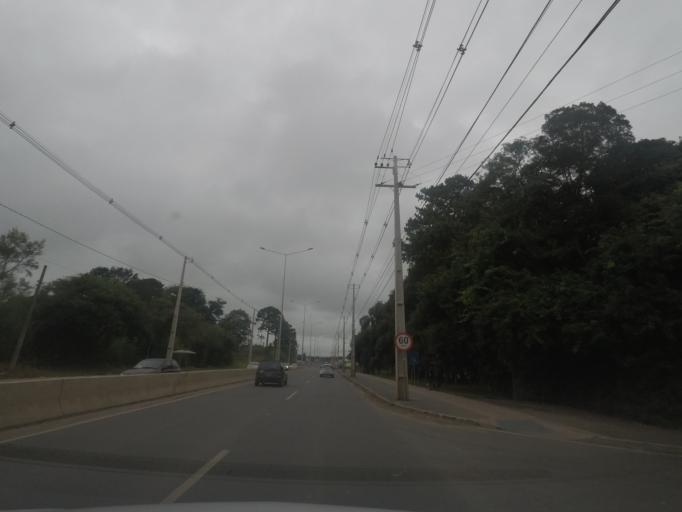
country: BR
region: Parana
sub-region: Piraquara
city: Piraquara
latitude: -25.4538
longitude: -49.0731
